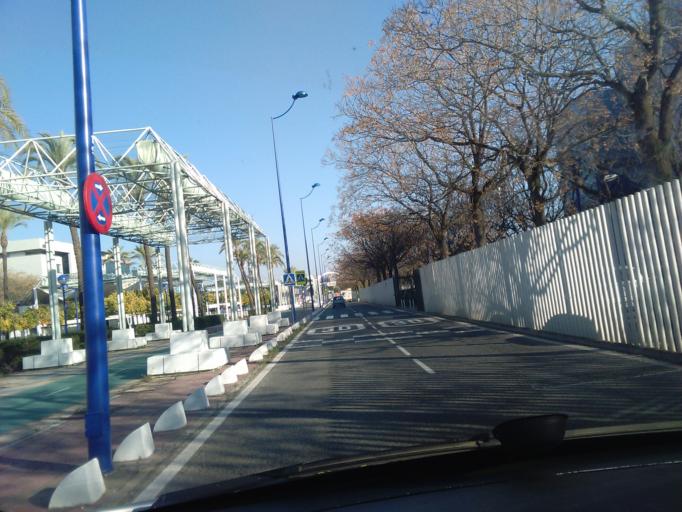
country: ES
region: Andalusia
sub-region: Provincia de Sevilla
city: Camas
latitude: 37.4058
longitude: -6.0060
